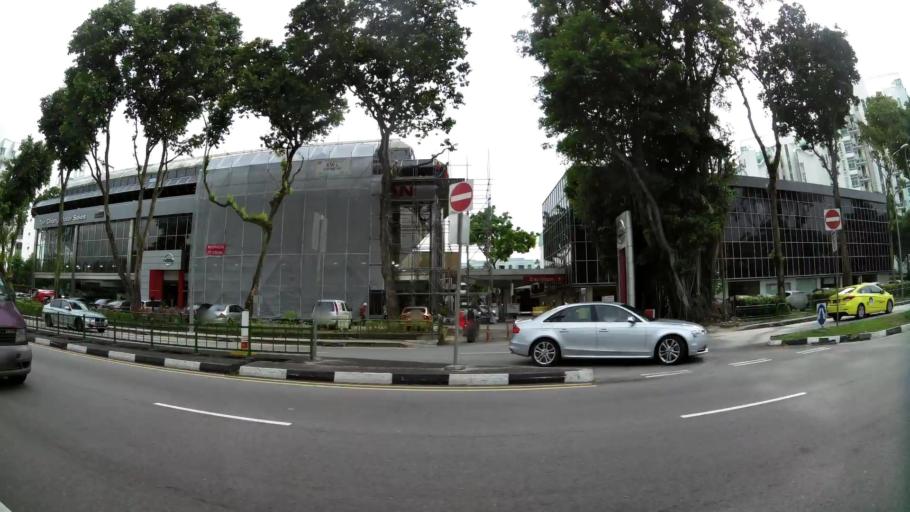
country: SG
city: Singapore
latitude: 1.3340
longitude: 103.7885
